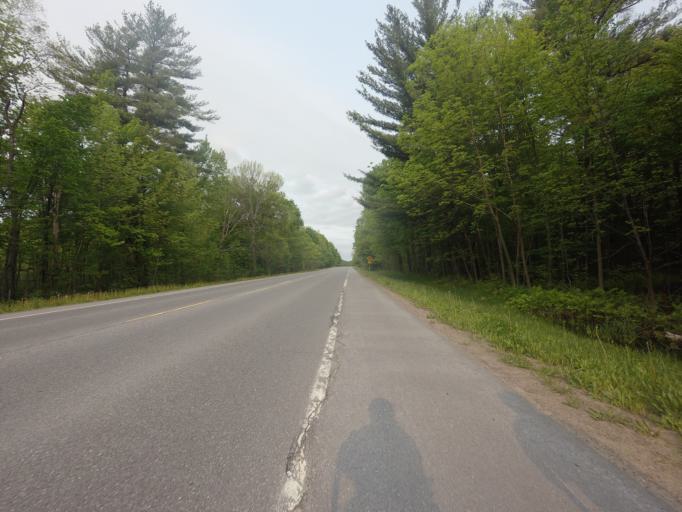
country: US
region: New York
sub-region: Jefferson County
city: Carthage
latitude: 44.0334
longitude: -75.5932
